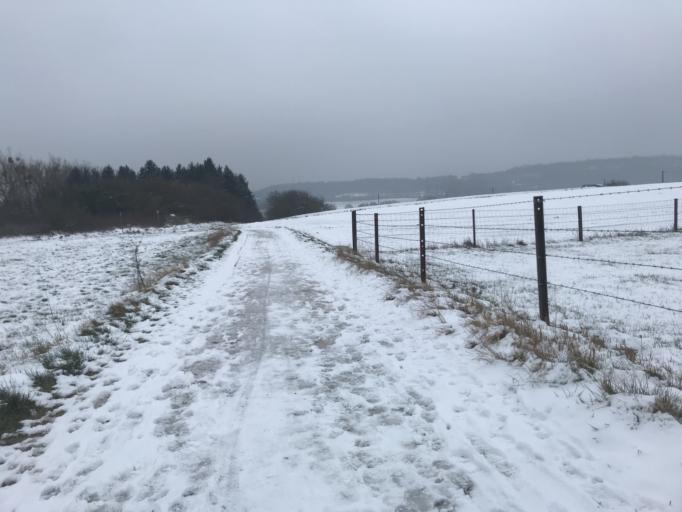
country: LU
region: Luxembourg
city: Belvaux
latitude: 49.4970
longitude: 5.9396
